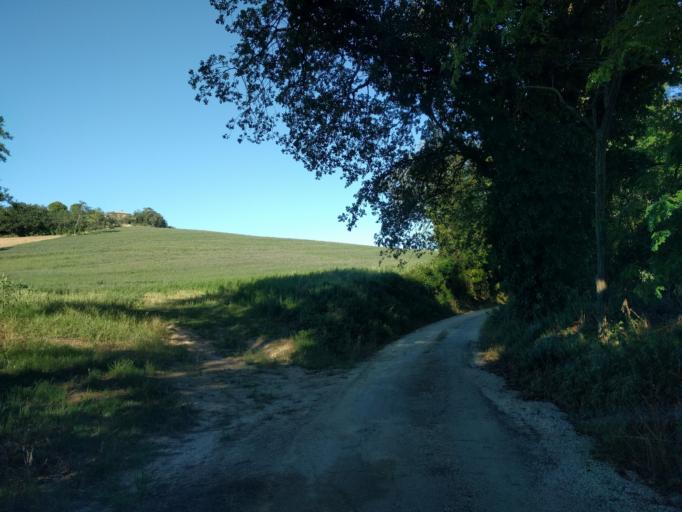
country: IT
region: The Marches
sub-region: Provincia di Pesaro e Urbino
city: Cuccurano
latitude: 43.8202
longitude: 12.9244
